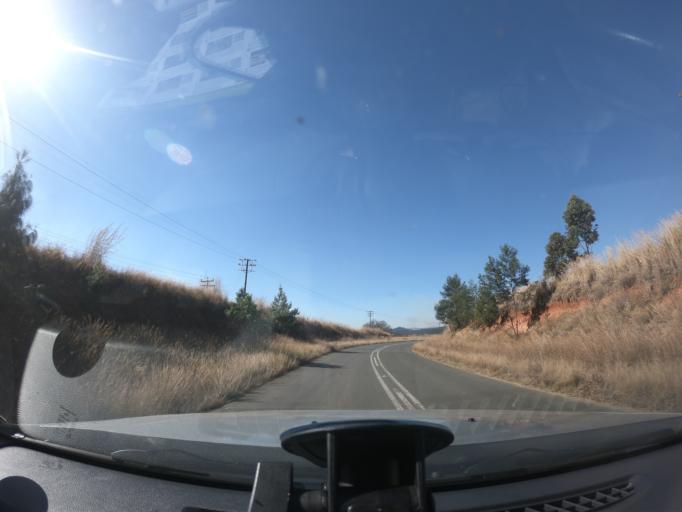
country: ZA
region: KwaZulu-Natal
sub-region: uMgungundlovu District Municipality
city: Howick
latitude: -29.4120
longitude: 30.0864
